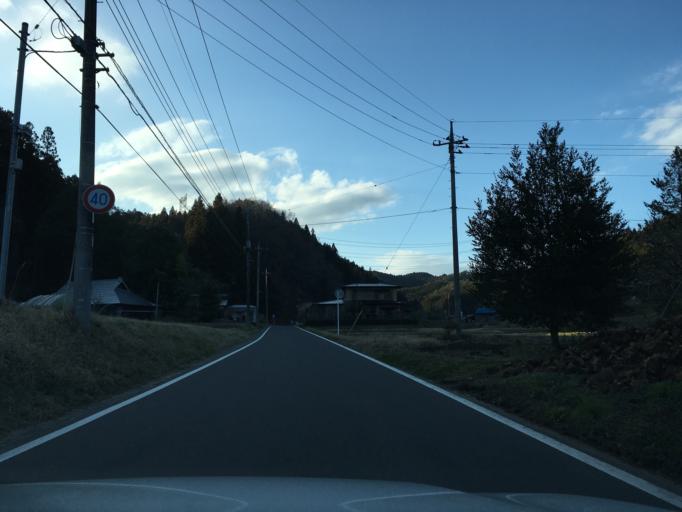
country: JP
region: Tochigi
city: Otawara
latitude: 36.8400
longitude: 140.1901
